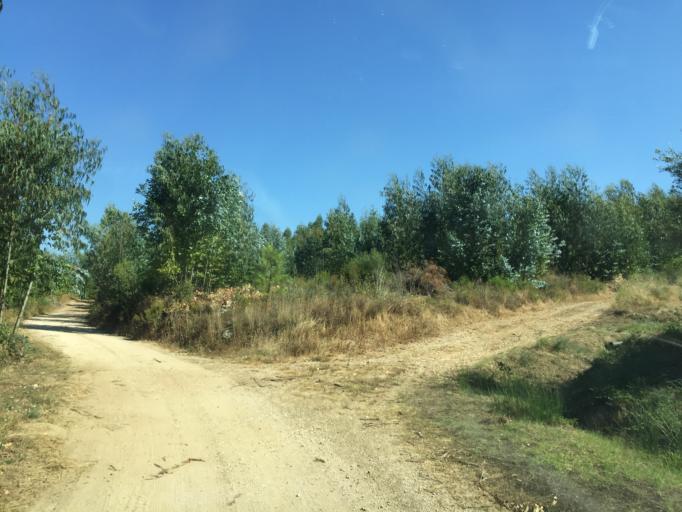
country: PT
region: Santarem
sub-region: Tomar
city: Tomar
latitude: 39.6072
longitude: -8.3485
